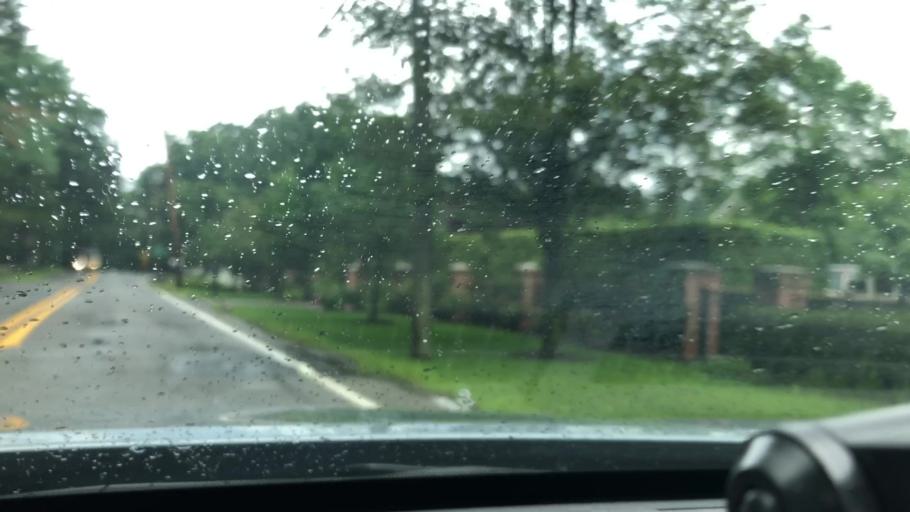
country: US
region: New Jersey
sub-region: Bergen County
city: Woodcliff Lake
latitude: 41.0353
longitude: -74.0675
